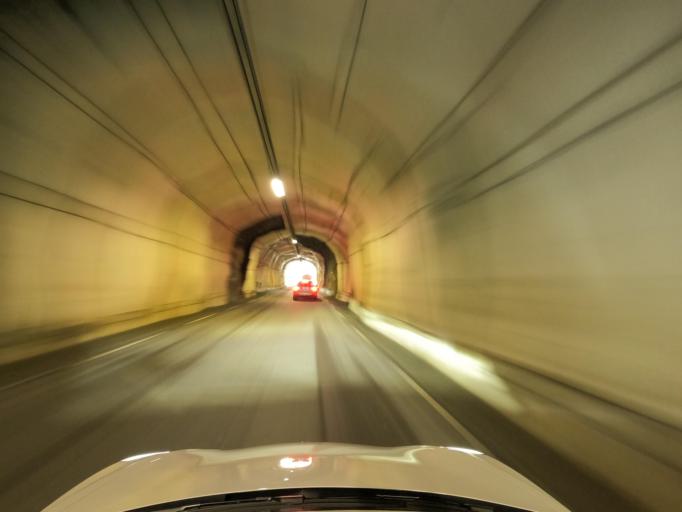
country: NO
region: Telemark
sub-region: Tinn
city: Rjukan
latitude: 59.8698
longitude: 8.4798
